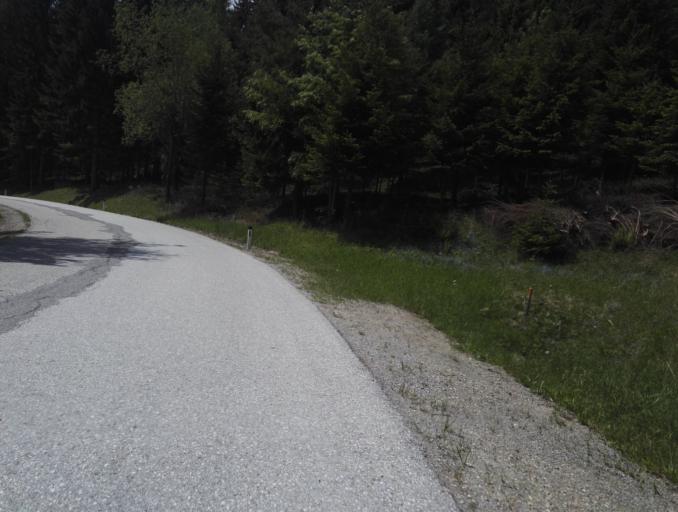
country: AT
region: Styria
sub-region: Politischer Bezirk Weiz
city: Stenzengreith
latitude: 47.2007
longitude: 15.4842
